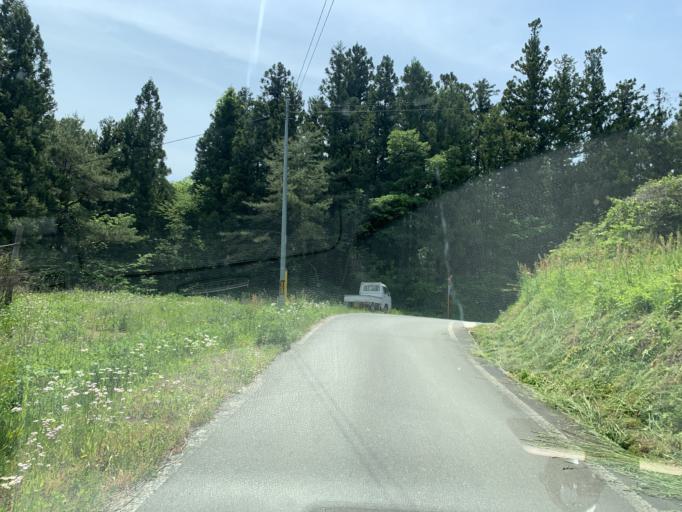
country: JP
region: Iwate
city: Ichinoseki
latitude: 38.9597
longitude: 141.2420
